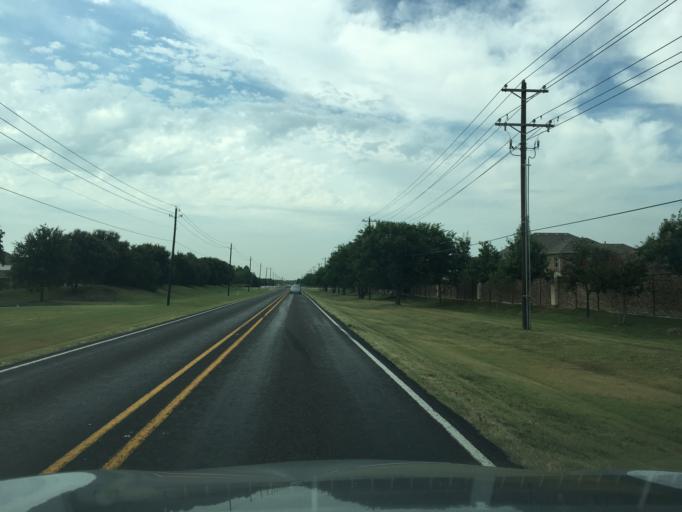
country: US
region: Texas
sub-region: Collin County
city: Parker
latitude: 33.0785
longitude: -96.6202
